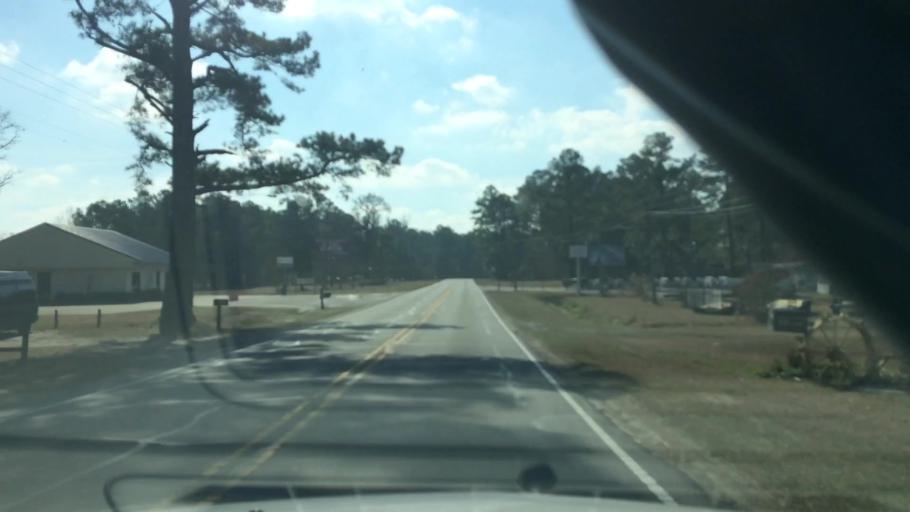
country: US
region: North Carolina
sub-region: Duplin County
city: Beulaville
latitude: 35.0622
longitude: -77.7400
